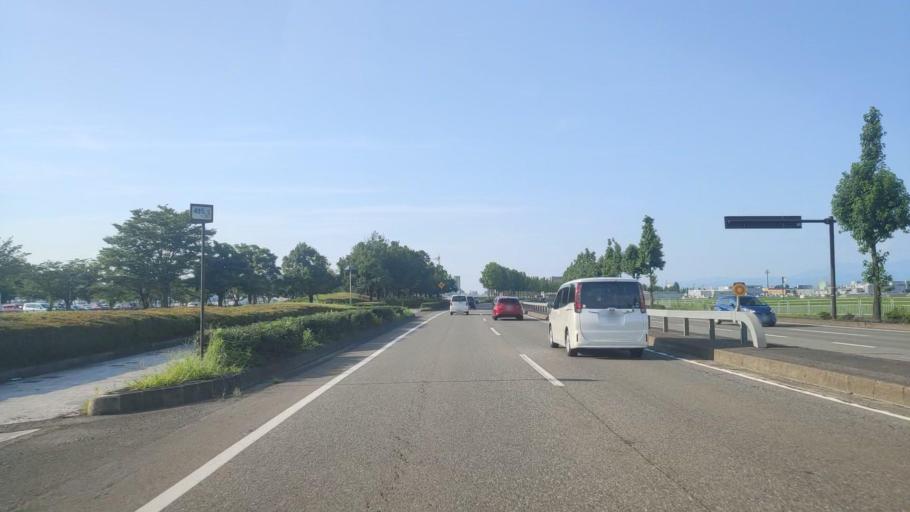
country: JP
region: Fukui
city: Fukui-shi
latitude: 36.0134
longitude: 136.2094
